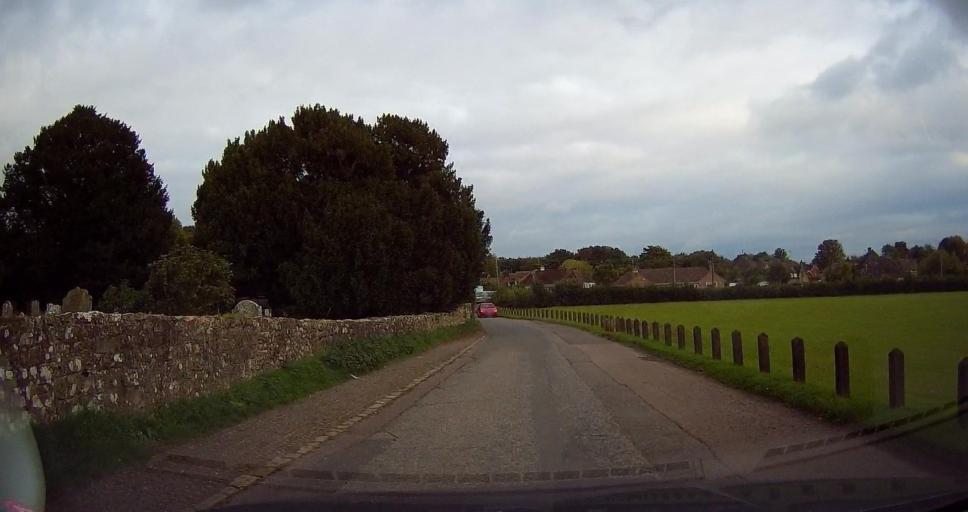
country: GB
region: England
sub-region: Kent
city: Harrietsham
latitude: 51.2451
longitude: 0.6848
